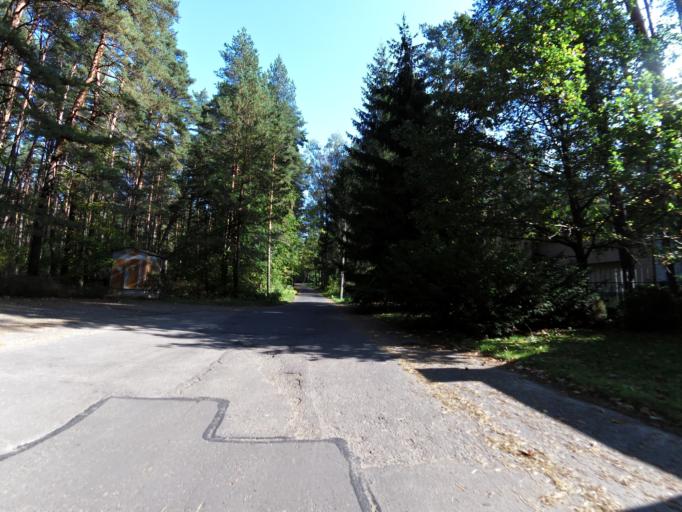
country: LT
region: Vilnius County
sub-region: Vilnius
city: Vilnius
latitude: 54.7332
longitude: 25.3051
